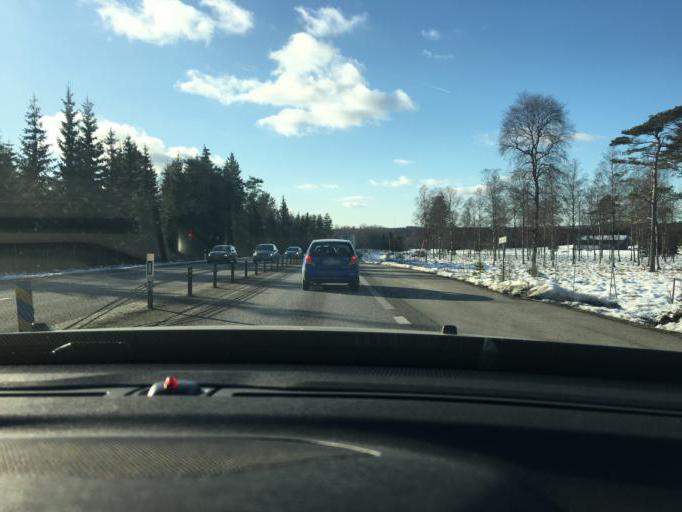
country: SE
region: Vaestra Goetaland
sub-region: Ulricehamns Kommun
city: Ulricehamn
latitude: 57.7956
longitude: 13.5541
